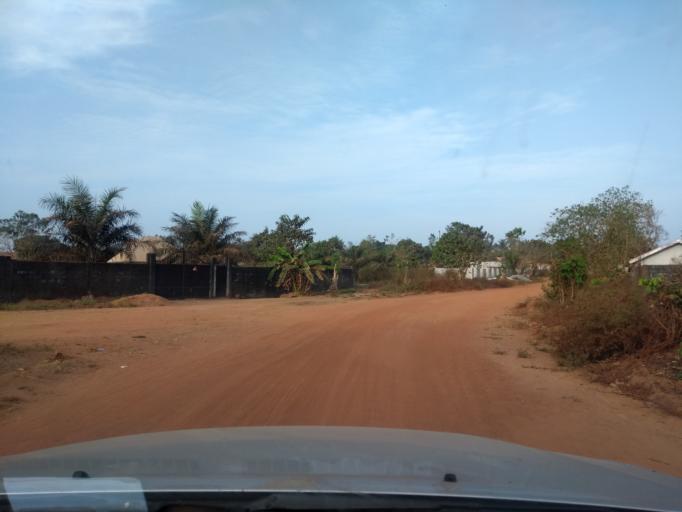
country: GN
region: Kindia
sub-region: Prefecture de Dubreka
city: Dubreka
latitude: 9.7868
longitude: -13.5367
